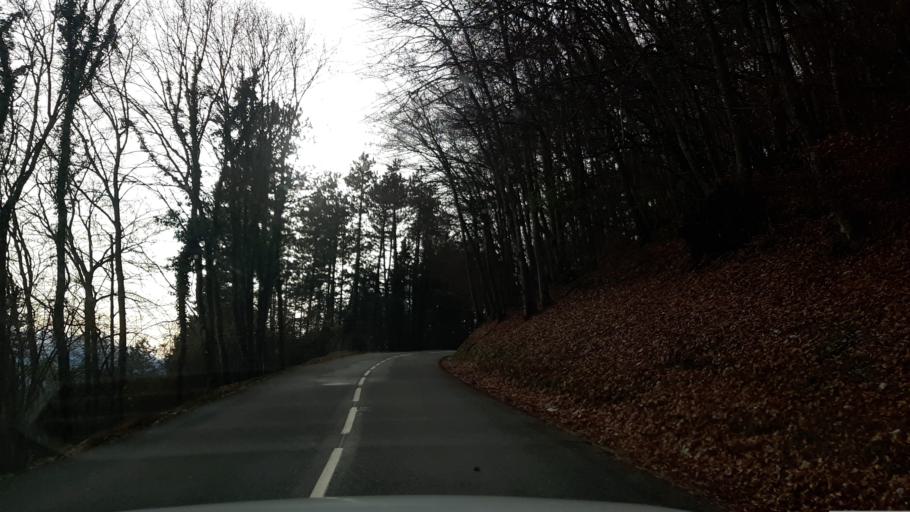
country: FR
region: Rhone-Alpes
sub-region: Departement de la Savoie
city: Coise-Saint-Jean-Pied-Gauthier
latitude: 45.5857
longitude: 6.1520
